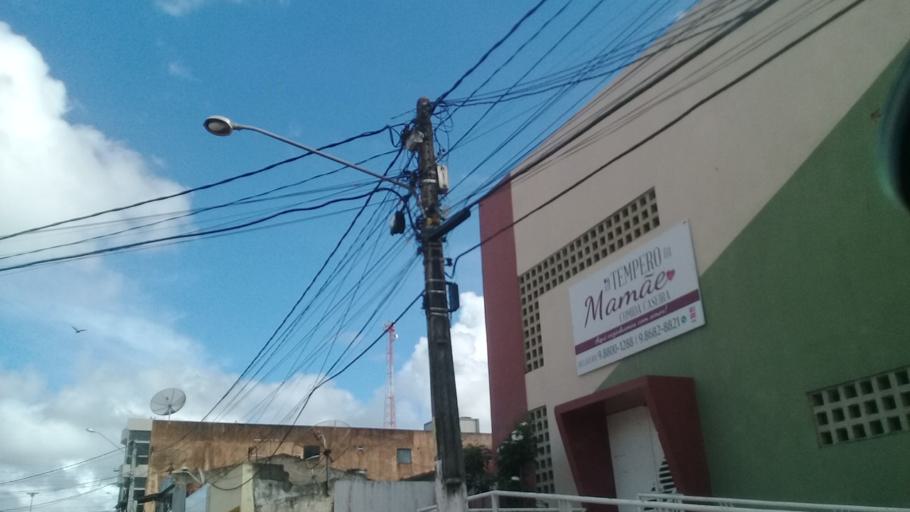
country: BR
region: Pernambuco
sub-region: Vitoria De Santo Antao
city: Vitoria de Santo Antao
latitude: -8.1288
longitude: -35.2953
